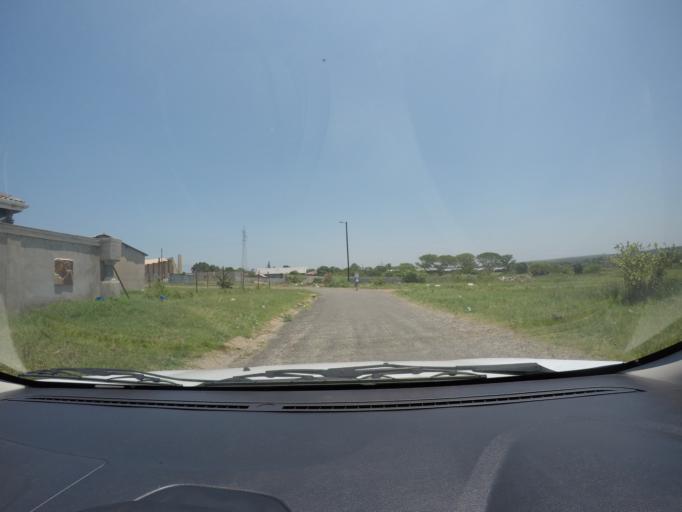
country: ZA
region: KwaZulu-Natal
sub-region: uThungulu District Municipality
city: eSikhawini
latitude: -28.8825
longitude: 31.8998
